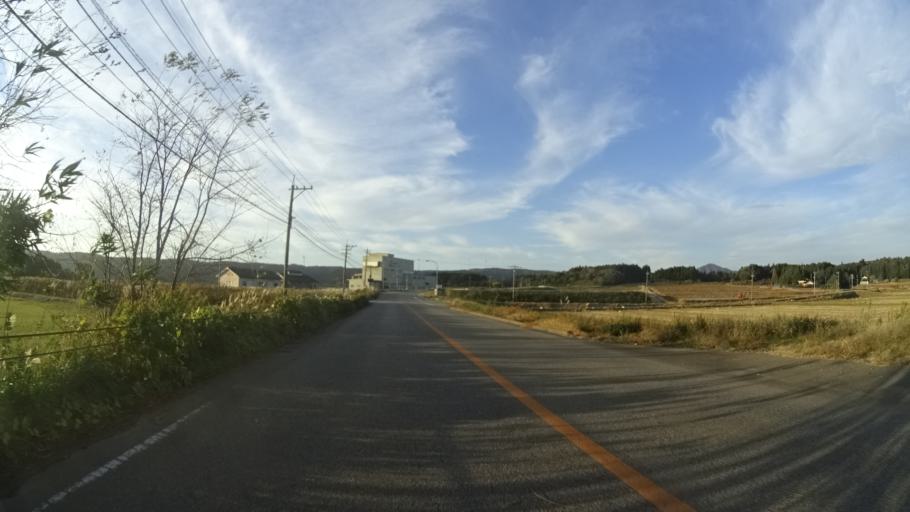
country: JP
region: Ishikawa
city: Nanao
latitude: 37.1583
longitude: 136.7178
